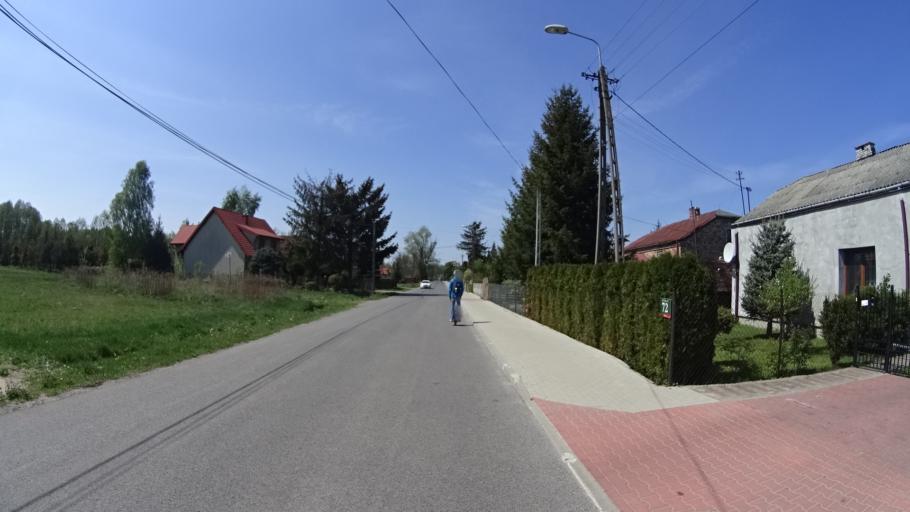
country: PL
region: Masovian Voivodeship
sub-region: Powiat warszawski zachodni
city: Truskaw
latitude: 52.2834
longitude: 20.7348
